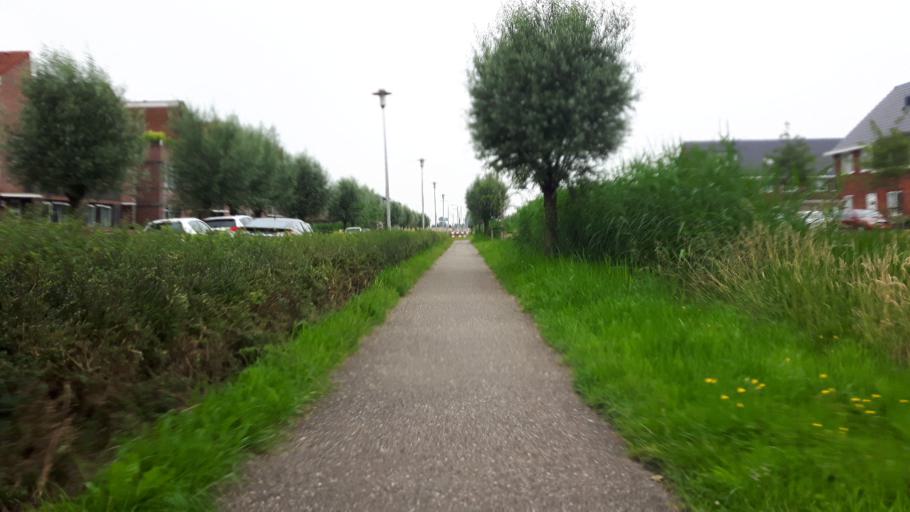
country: NL
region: South Holland
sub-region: Gemeente Schoonhoven
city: Schoonhoven
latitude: 51.9473
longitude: 4.8694
